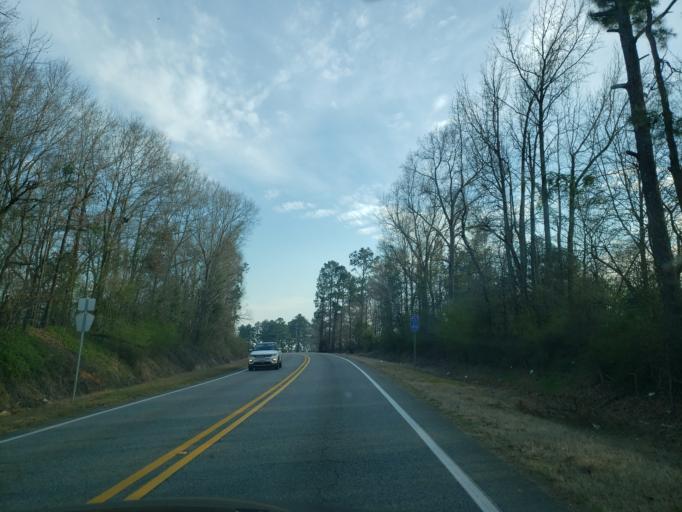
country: US
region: Alabama
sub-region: Hale County
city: Moundville
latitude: 32.9677
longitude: -87.6252
